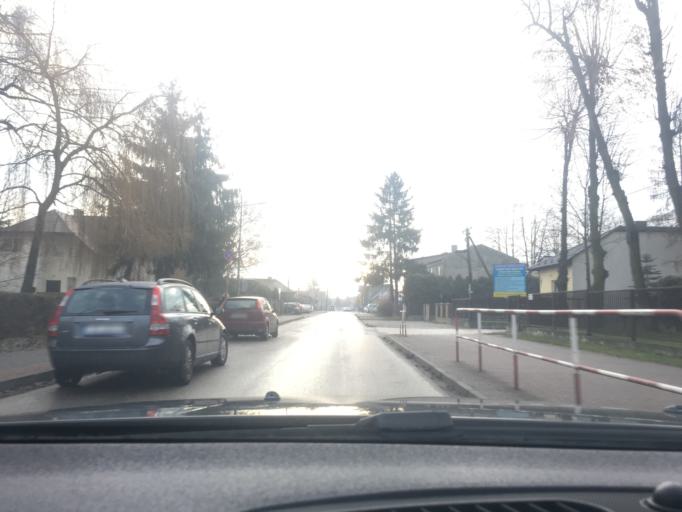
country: PL
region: Swietokrzyskie
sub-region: Powiat jedrzejowski
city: Jedrzejow
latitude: 50.6462
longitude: 20.2921
